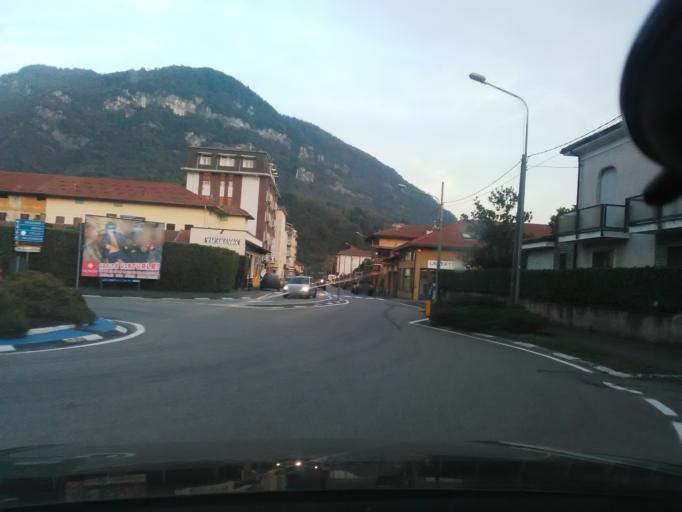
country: IT
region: Piedmont
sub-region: Provincia di Vercelli
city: Borgosesia
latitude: 45.7105
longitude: 8.2935
